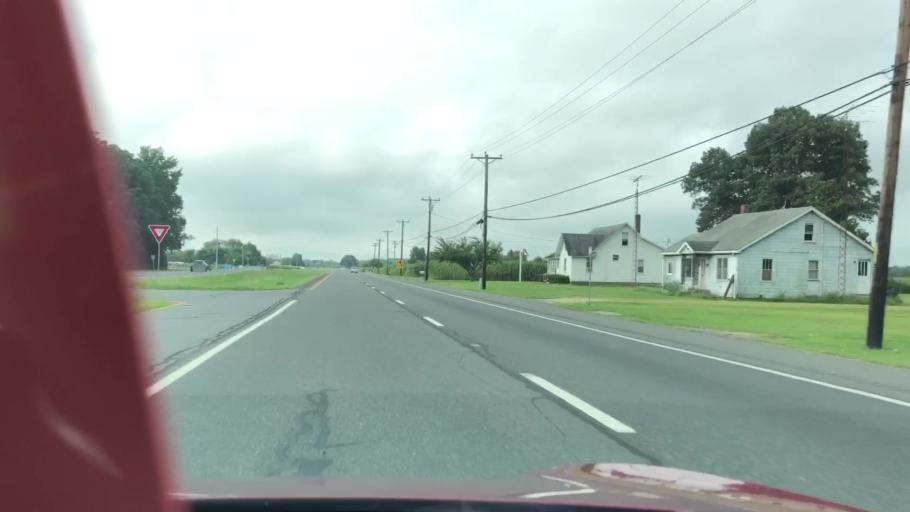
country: US
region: Delaware
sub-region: Kent County
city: Harrington
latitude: 38.8908
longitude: -75.5723
